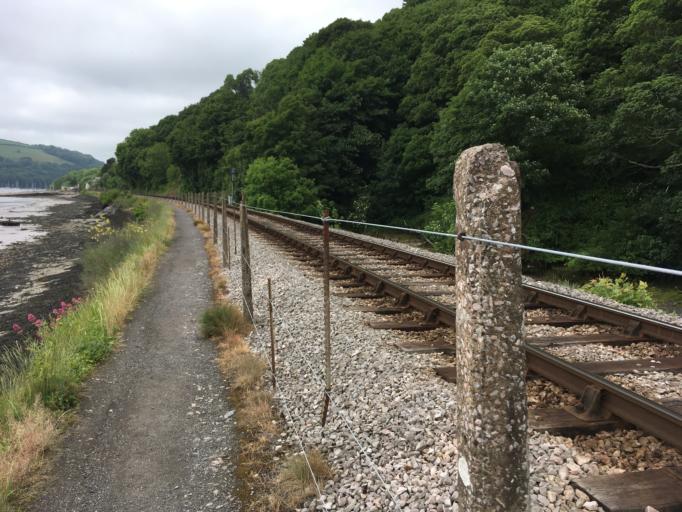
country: GB
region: England
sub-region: Devon
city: Dartmouth
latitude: 50.3567
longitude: -3.5704
